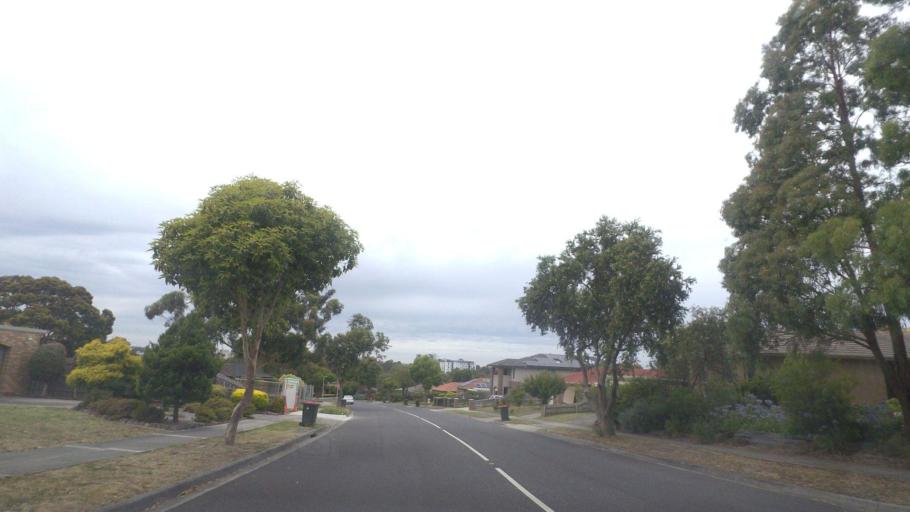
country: AU
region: Victoria
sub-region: Knox
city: Wantirna
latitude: -37.8640
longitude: 145.2335
